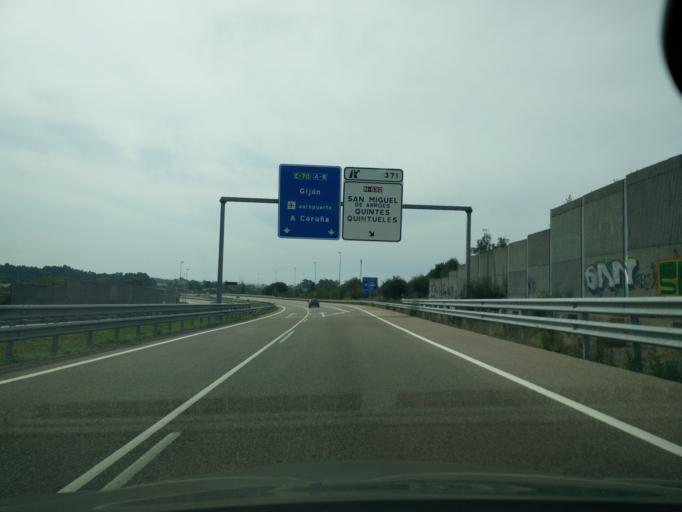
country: ES
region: Asturias
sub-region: Province of Asturias
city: Arriba
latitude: 43.5115
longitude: -5.5641
